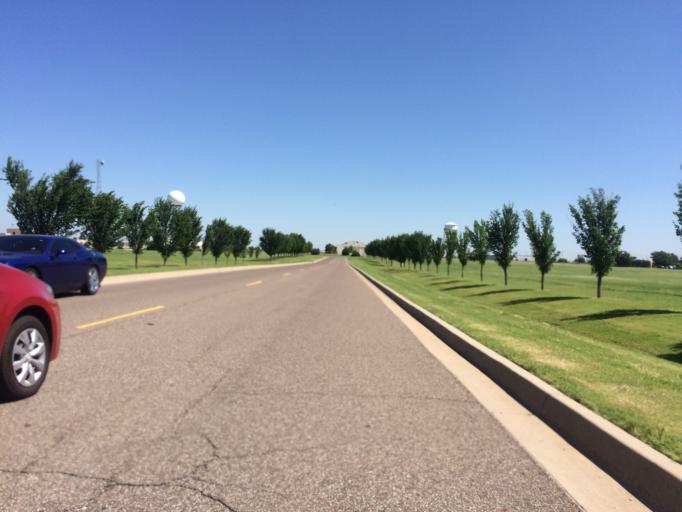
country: US
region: Oklahoma
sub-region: Cleveland County
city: Norman
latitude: 35.2346
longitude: -97.4590
